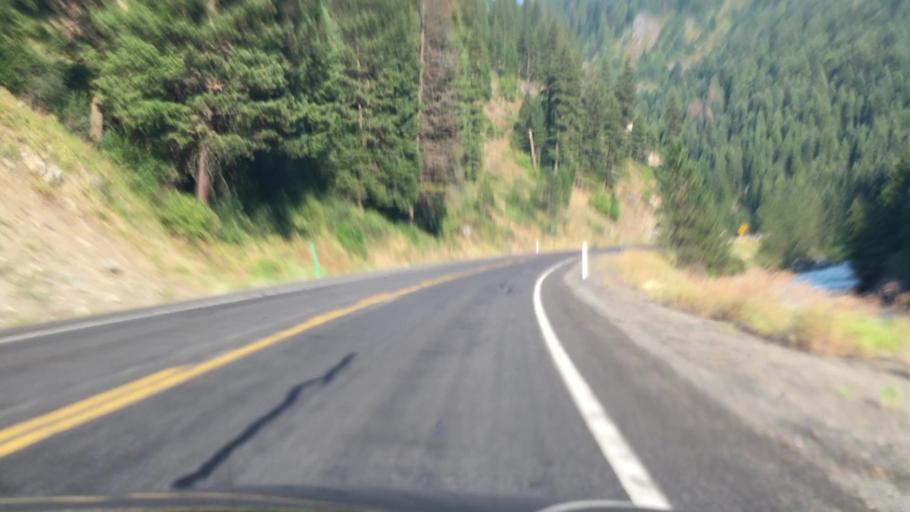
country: US
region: Idaho
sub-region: Valley County
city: Cascade
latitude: 44.2632
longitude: -116.0739
